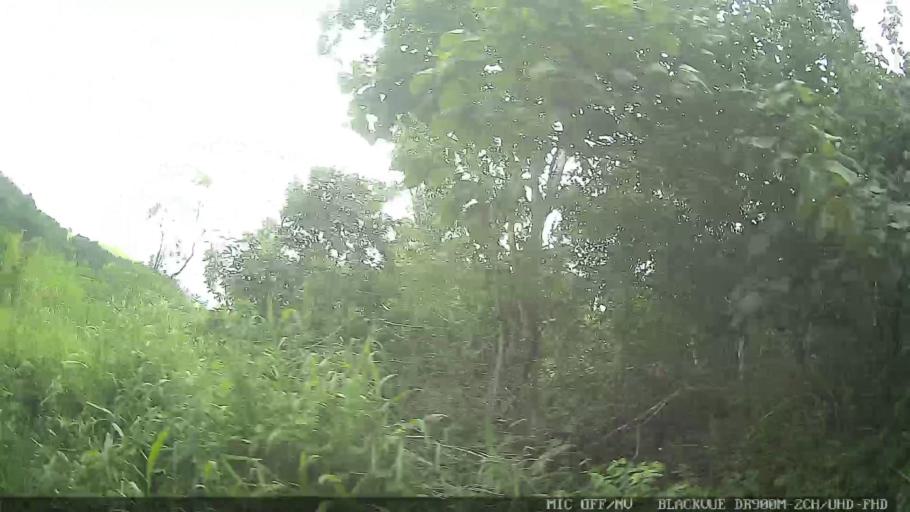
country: BR
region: Sao Paulo
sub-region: Santa Isabel
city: Santa Isabel
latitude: -23.3716
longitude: -46.2500
